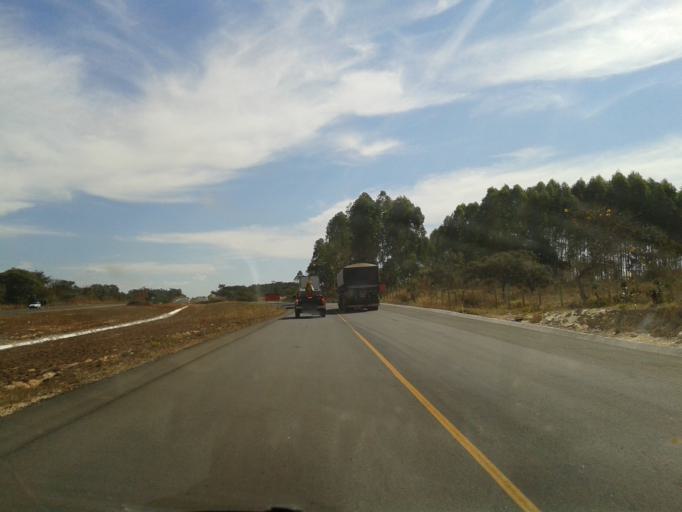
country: BR
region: Goias
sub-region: Goias
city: Goias
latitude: -16.0026
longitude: -50.0549
